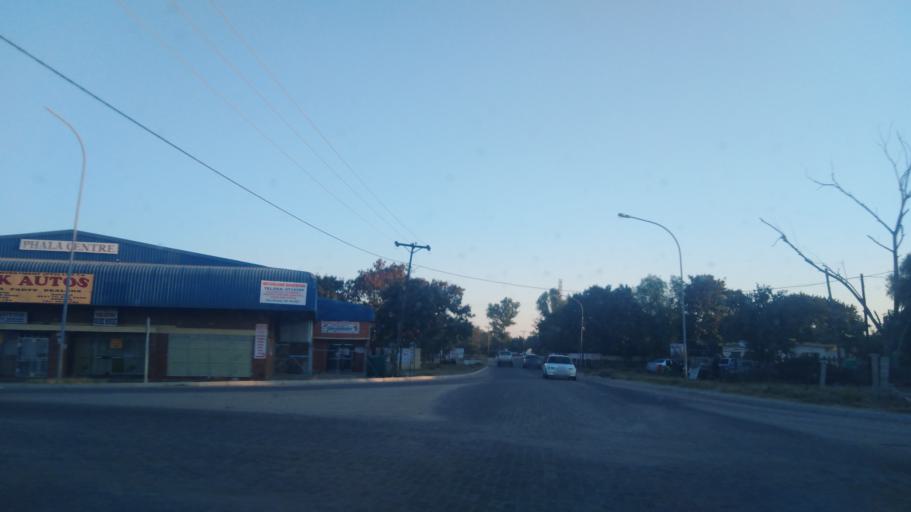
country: BW
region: Central
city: Mahalapye
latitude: -23.1116
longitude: 26.8321
